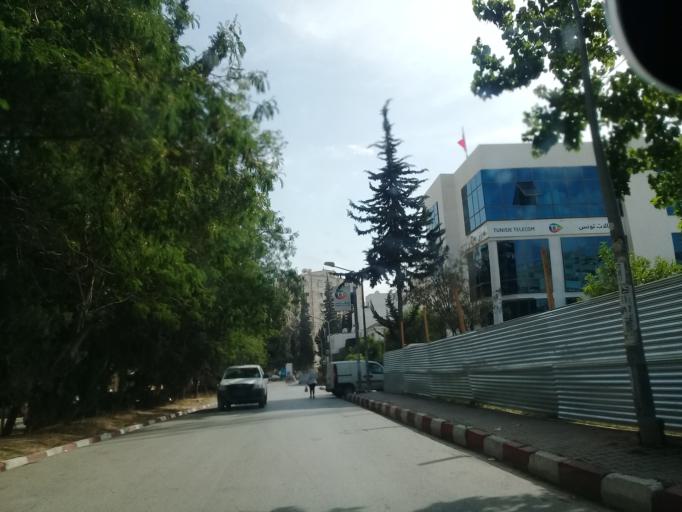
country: TN
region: Tunis
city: Tunis
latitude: 36.8457
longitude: 10.1663
